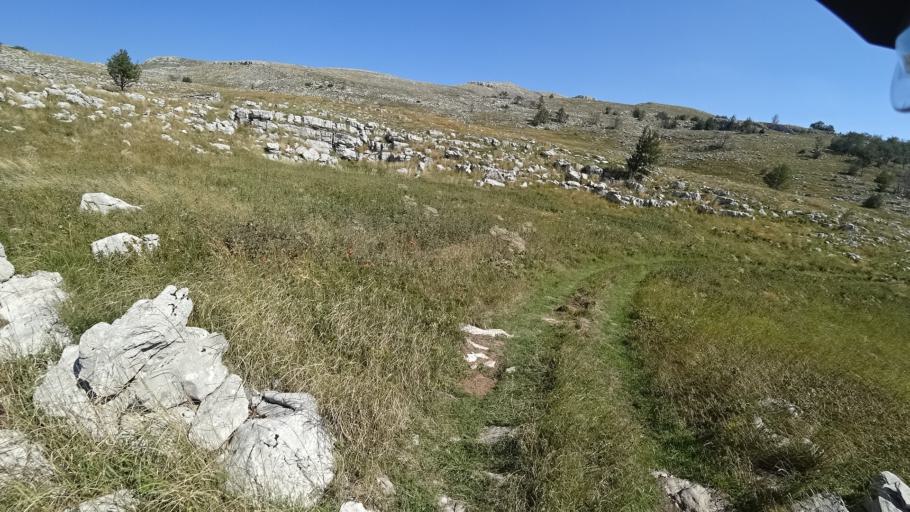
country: HR
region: Splitsko-Dalmatinska
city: Hrvace
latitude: 43.9208
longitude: 16.6056
